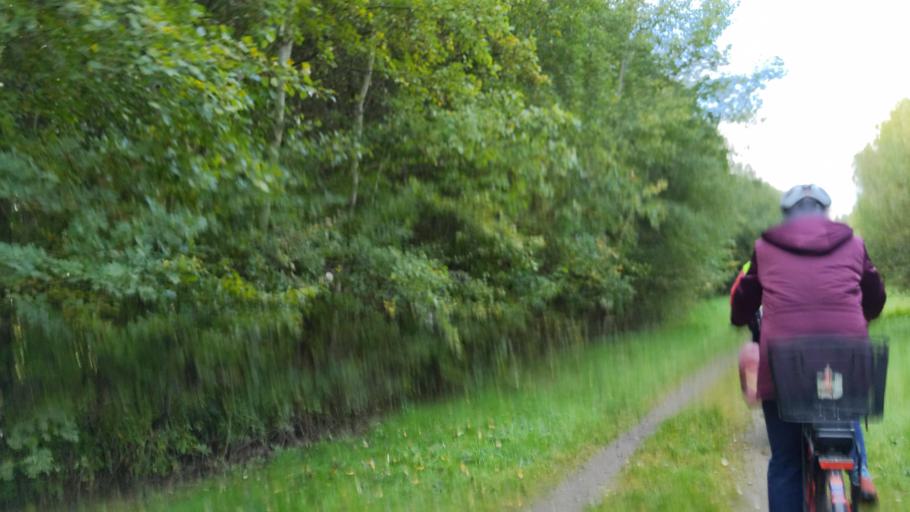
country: DE
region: Schleswig-Holstein
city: Badendorf
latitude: 53.8787
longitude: 10.5920
